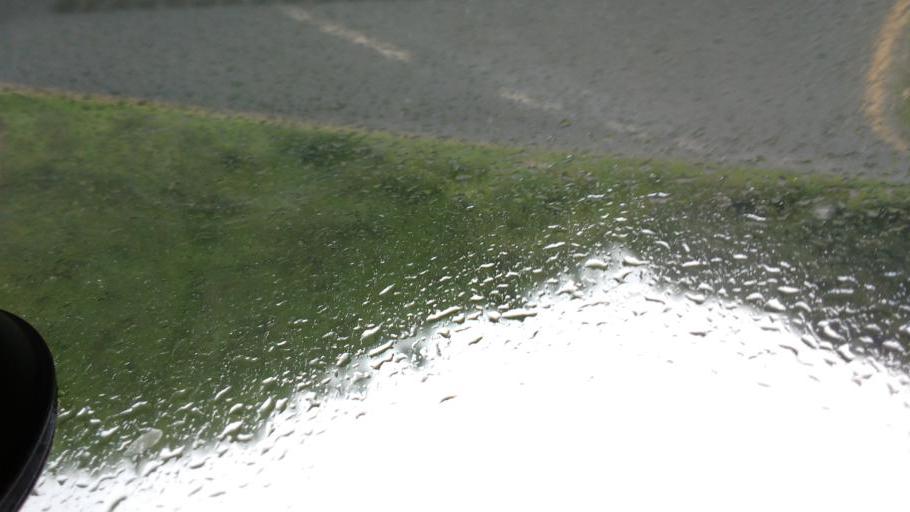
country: IN
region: Meghalaya
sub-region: East Khasi Hills
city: Shillong
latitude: 25.4529
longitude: 91.8191
